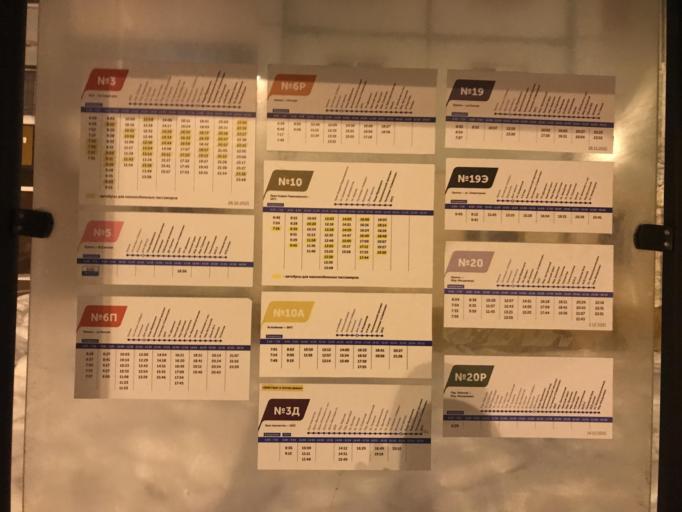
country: RU
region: Tjumen
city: Tobol'sk
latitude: 58.2109
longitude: 68.2720
